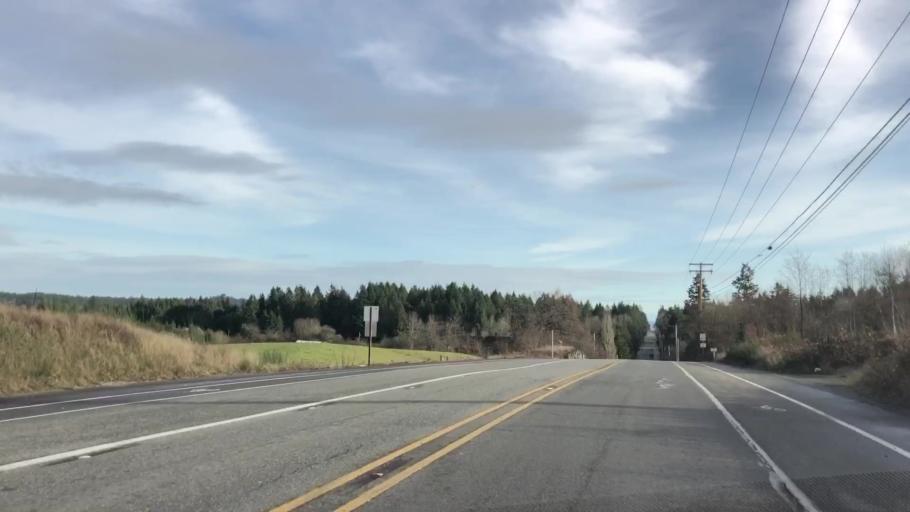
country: US
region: Washington
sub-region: Kitsap County
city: Kingston
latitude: 47.7950
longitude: -122.5411
